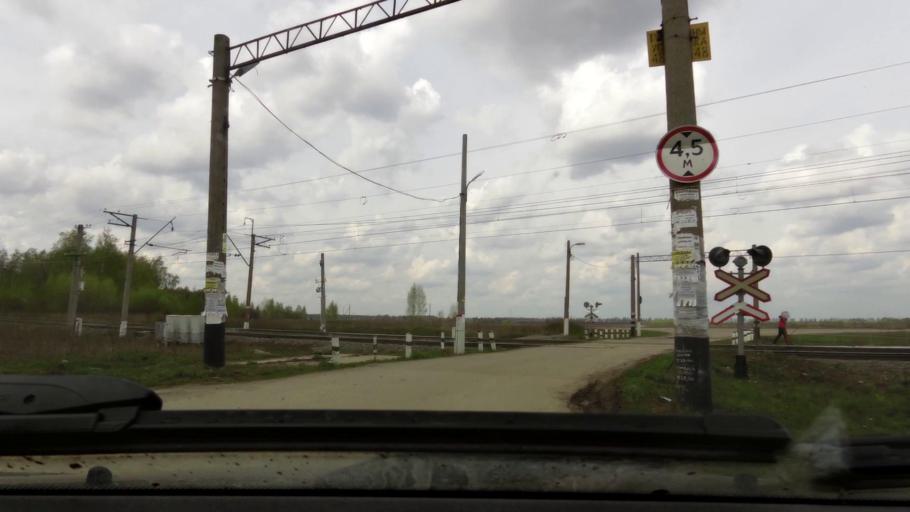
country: RU
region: Rjazan
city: Bagramovo
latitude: 54.7070
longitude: 39.3147
